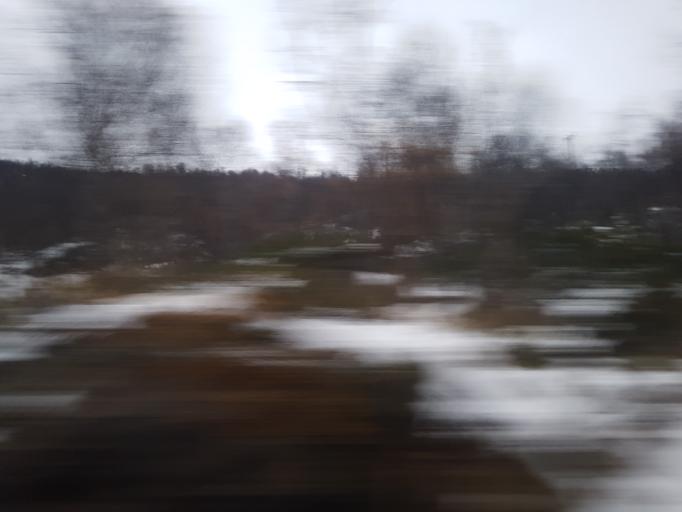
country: NO
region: Sor-Trondelag
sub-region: Oppdal
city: Oppdal
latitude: 62.3037
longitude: 9.6046
